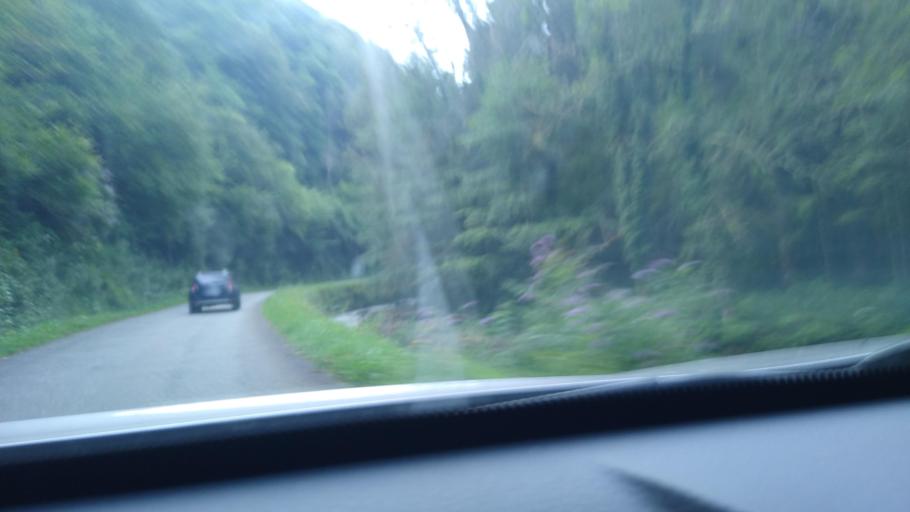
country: FR
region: Midi-Pyrenees
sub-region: Departement de l'Ariege
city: Saint-Girons
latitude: 42.8075
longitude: 1.1962
